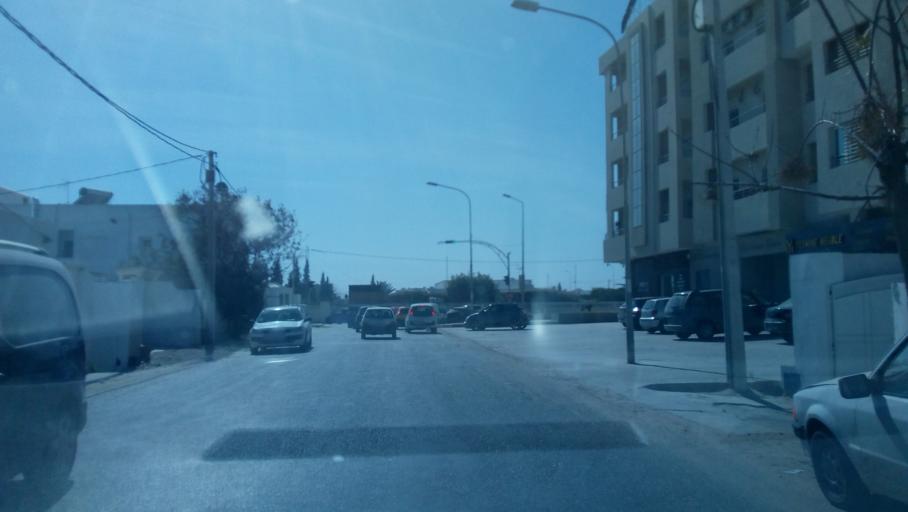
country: TN
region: Safaqis
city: Sfax
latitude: 34.7658
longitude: 10.7257
